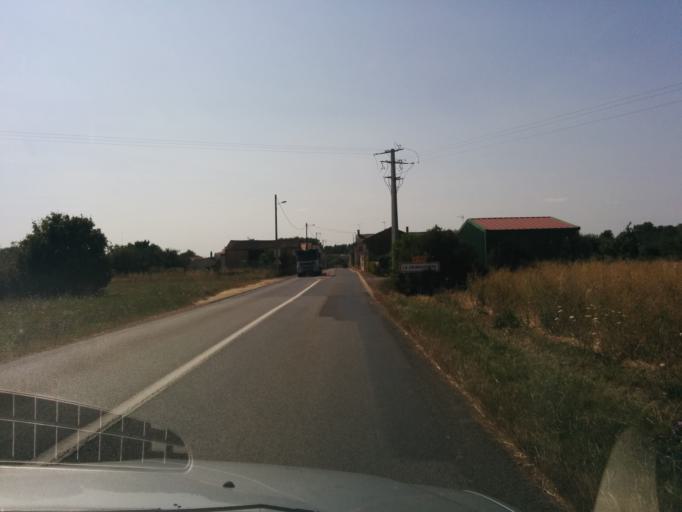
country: FR
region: Poitou-Charentes
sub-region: Departement de la Vienne
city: Saint-Jean-de-Sauves
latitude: 46.8060
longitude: 0.0227
